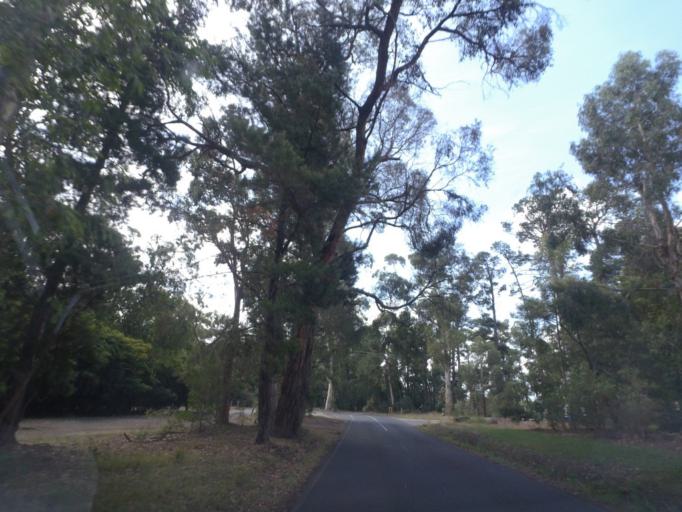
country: AU
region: Victoria
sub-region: Yarra Ranges
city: Montrose
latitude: -37.7874
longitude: 145.3535
